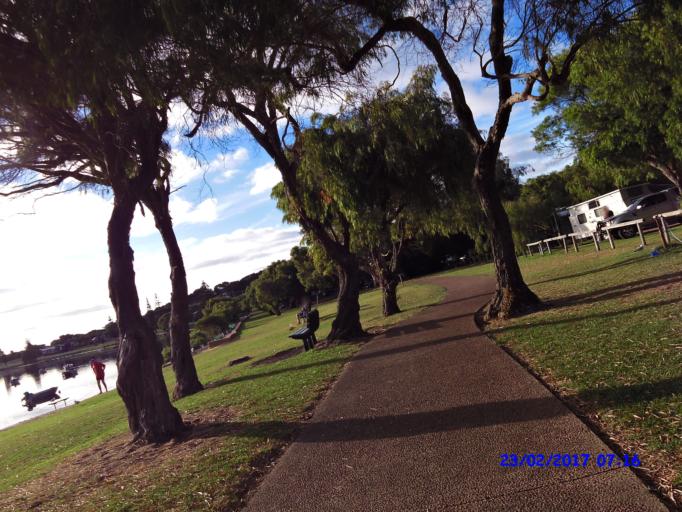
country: AU
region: Western Australia
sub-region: Augusta-Margaret River Shire
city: Augusta
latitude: -34.3230
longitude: 115.1645
